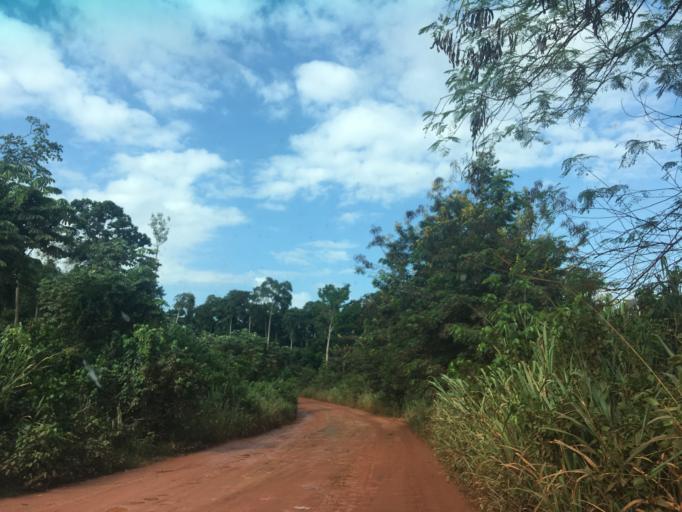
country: GH
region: Western
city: Wassa-Akropong
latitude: 5.9614
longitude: -2.4263
